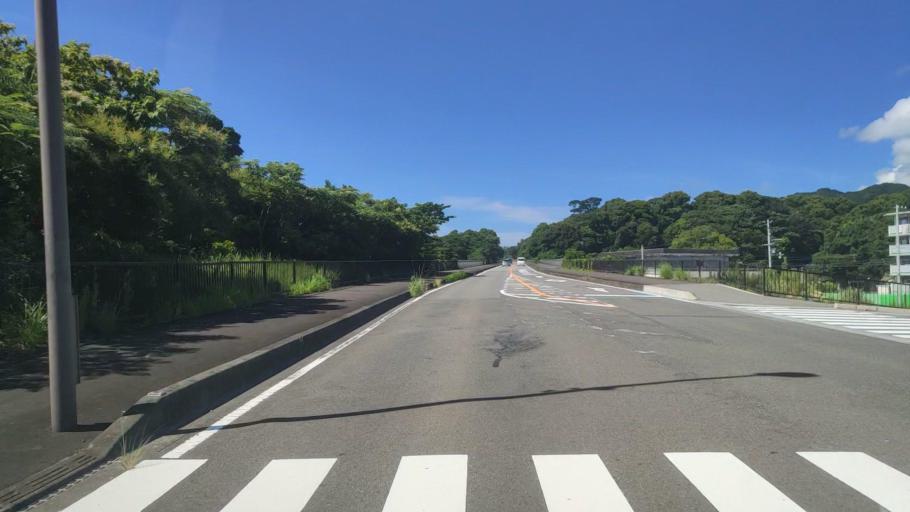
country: JP
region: Wakayama
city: Shingu
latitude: 33.7114
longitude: 135.9984
